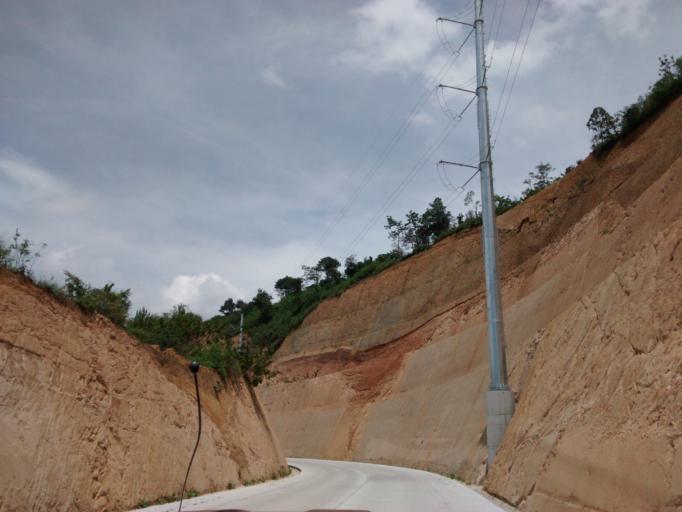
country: GT
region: Sacatepequez
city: Santo Domingo Xenacoj
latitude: 14.6919
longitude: -90.7135
